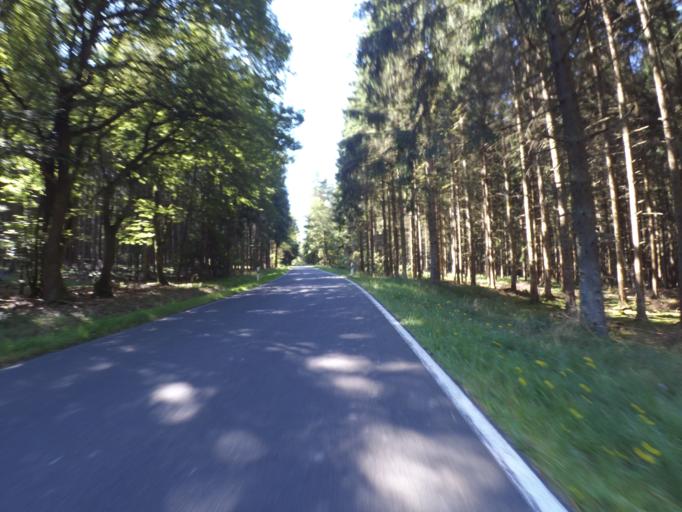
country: DE
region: Rheinland-Pfalz
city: Demerath
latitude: 50.1932
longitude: 6.9512
